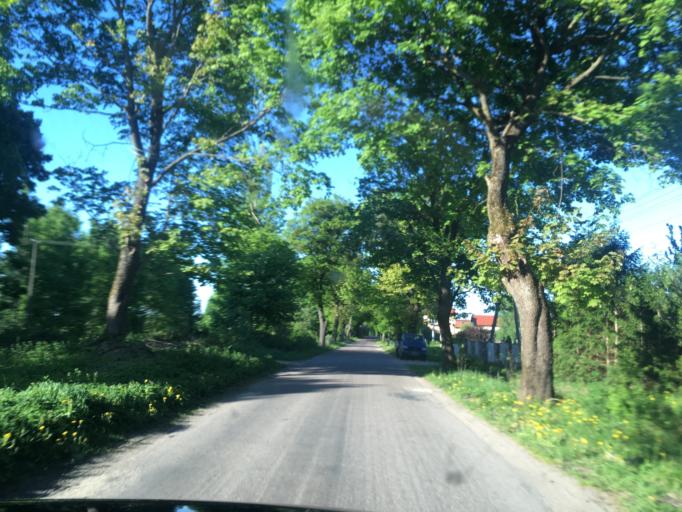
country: PL
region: Warmian-Masurian Voivodeship
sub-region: Powiat piski
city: Ruciane-Nida
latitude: 53.6794
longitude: 21.4954
